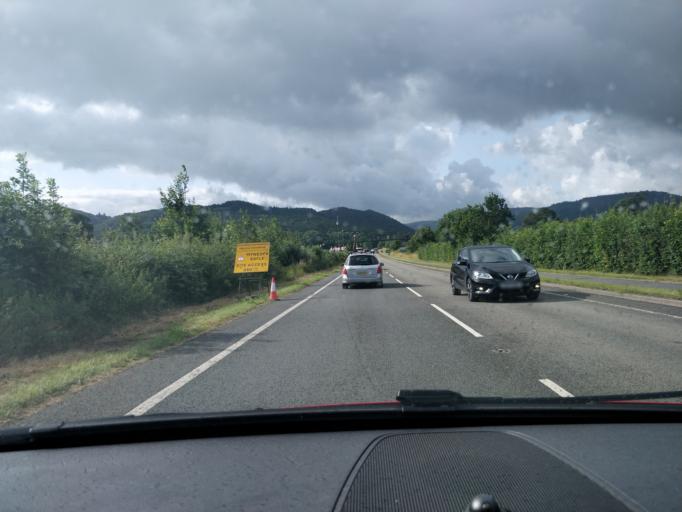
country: GB
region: Wales
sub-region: Conwy
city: Llanrwst
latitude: 53.1161
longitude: -3.7811
